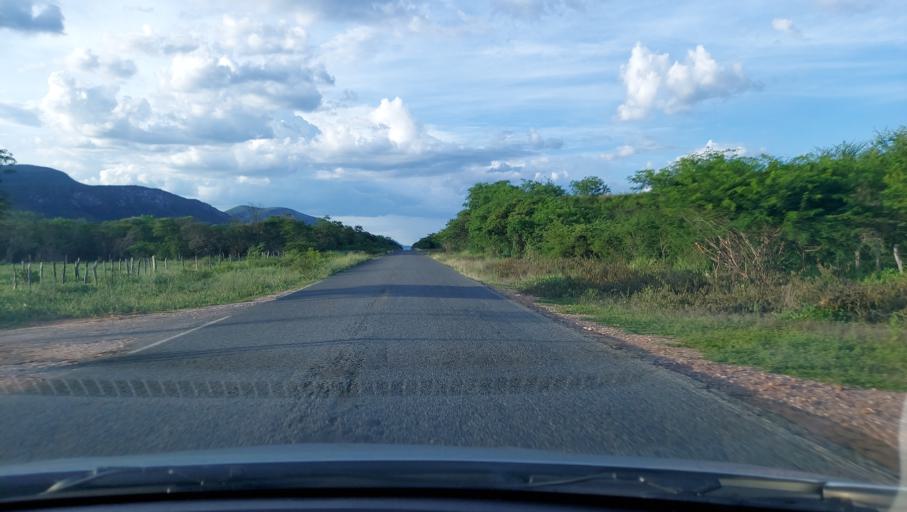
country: BR
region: Bahia
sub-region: Oliveira Dos Brejinhos
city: Beira Rio
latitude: -12.1856
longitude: -42.5400
